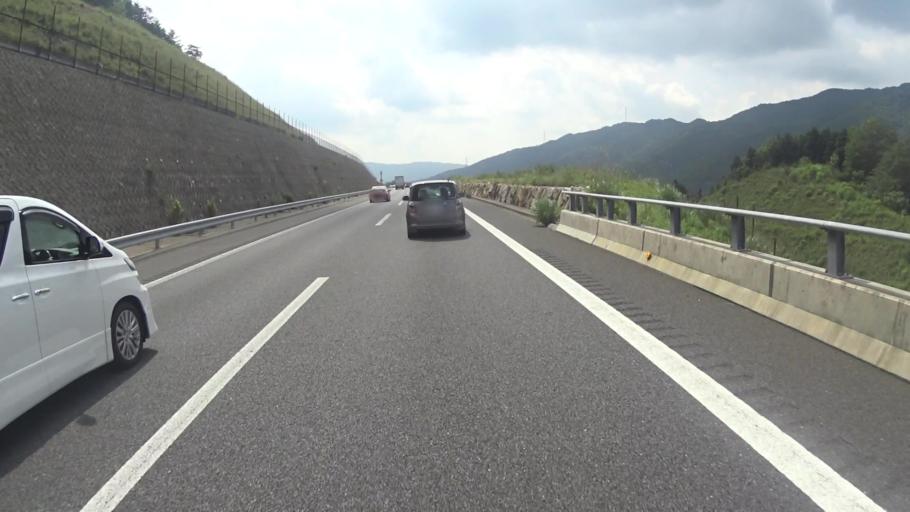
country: JP
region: Shiga Prefecture
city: Kusatsu
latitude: 34.9353
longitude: 136.0408
